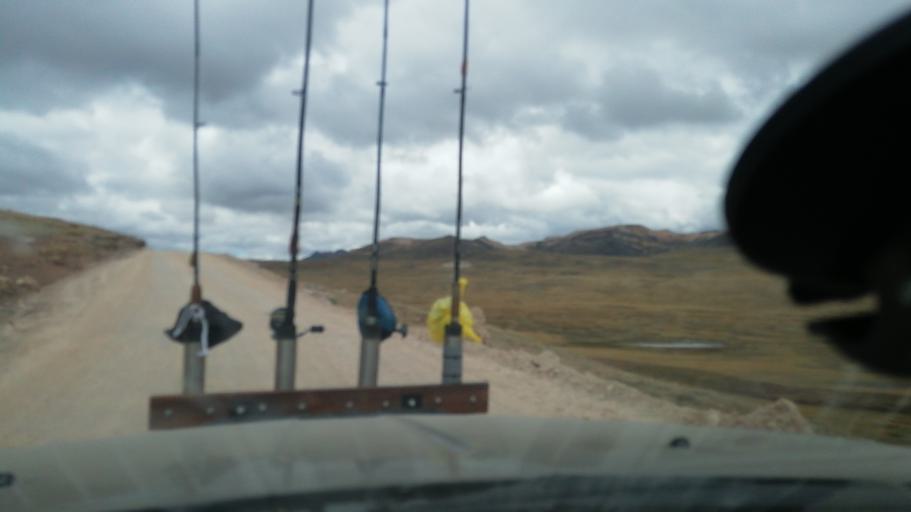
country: PE
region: Huancavelica
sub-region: Provincia de Huancavelica
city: Acobambilla
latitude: -12.5376
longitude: -75.5547
